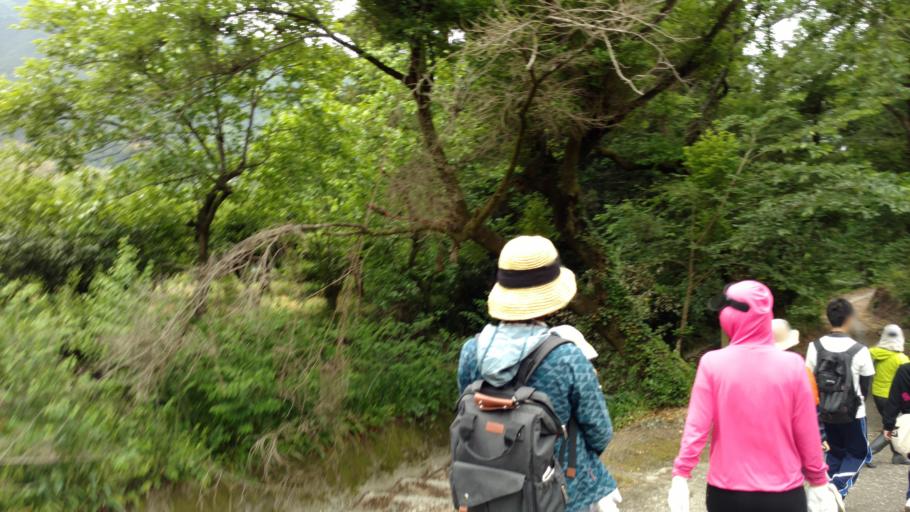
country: JP
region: Ehime
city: Saijo
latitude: 33.8654
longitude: 133.1990
